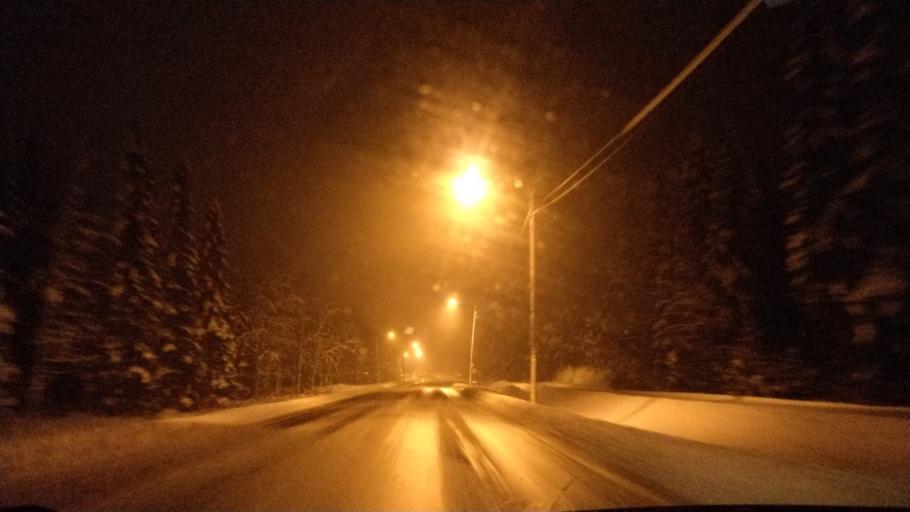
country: FI
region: Lapland
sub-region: Rovaniemi
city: Rovaniemi
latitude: 66.2777
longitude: 25.3328
